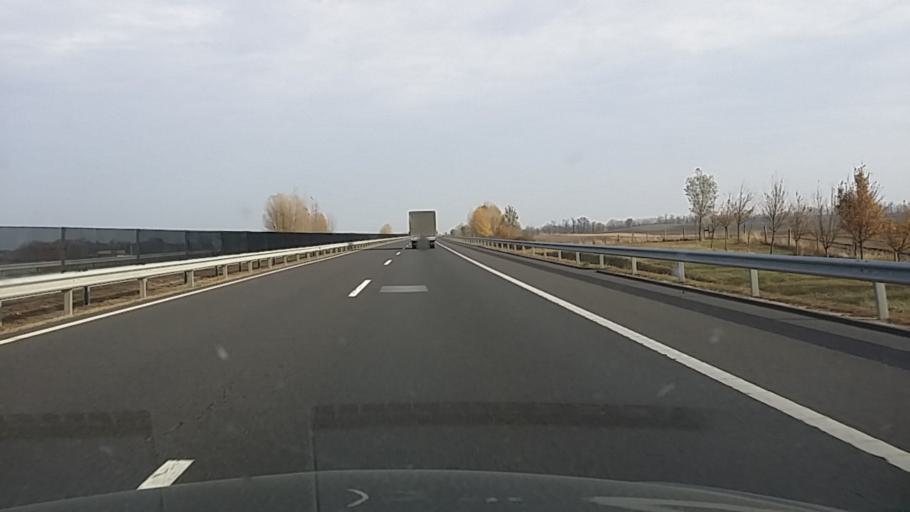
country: HU
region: Szabolcs-Szatmar-Bereg
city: Nagycserkesz
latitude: 47.9027
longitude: 21.5169
